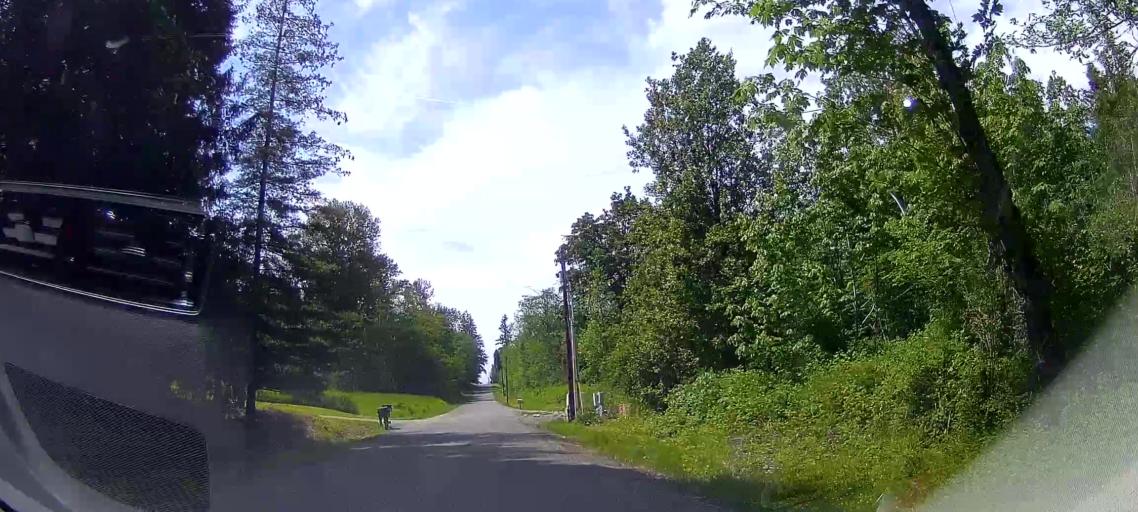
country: US
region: Washington
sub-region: Skagit County
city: Mount Vernon
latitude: 48.4065
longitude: -122.2982
